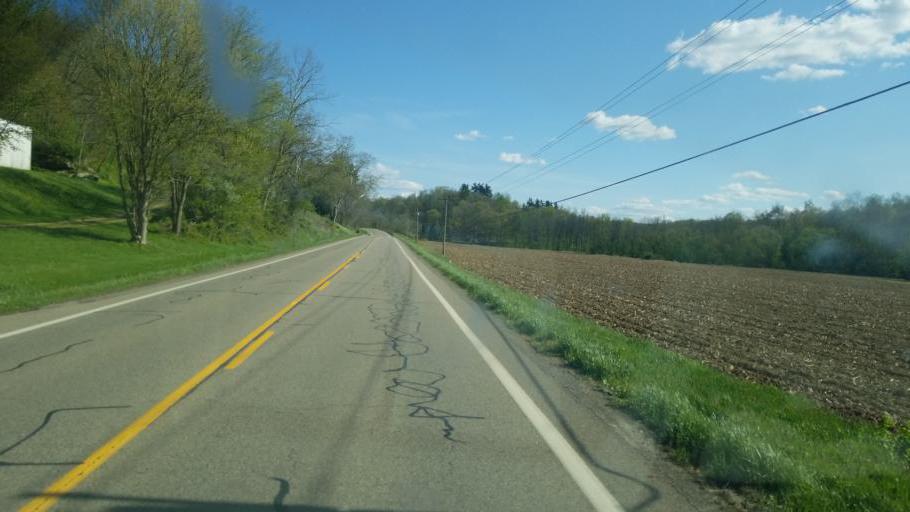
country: US
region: Ohio
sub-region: Coshocton County
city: Coshocton
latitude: 40.3449
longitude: -81.8828
